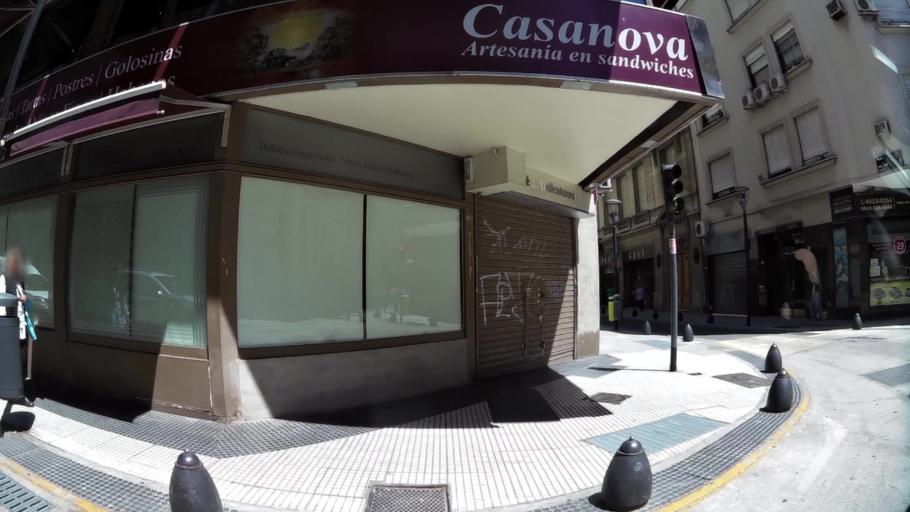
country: AR
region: Buenos Aires F.D.
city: Retiro
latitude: -34.5964
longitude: -58.3769
